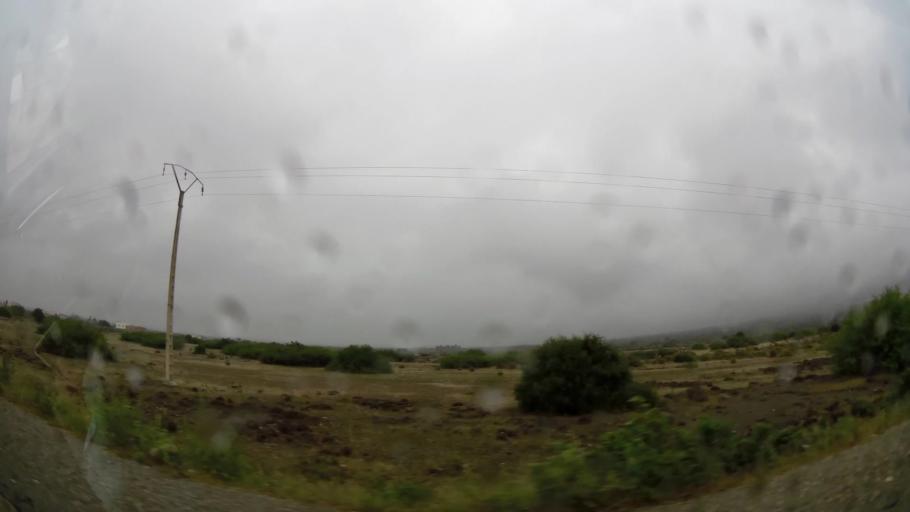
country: MA
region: Taza-Al Hoceima-Taounate
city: Imzourene
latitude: 35.1410
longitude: -3.7918
